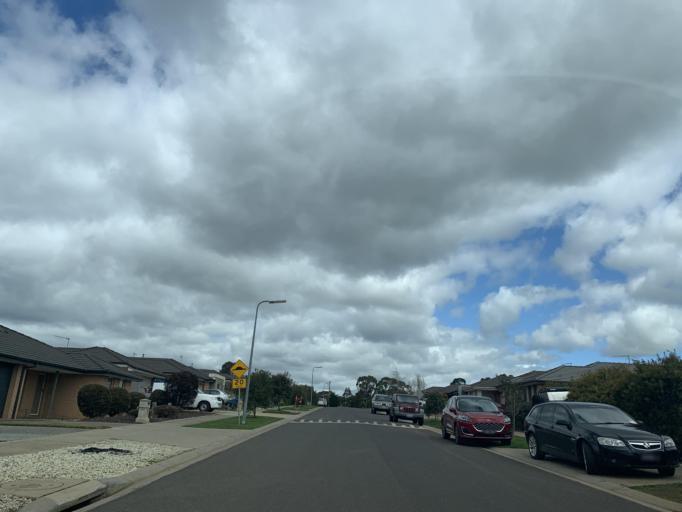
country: AU
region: Victoria
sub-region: Whittlesea
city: Whittlesea
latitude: -37.2921
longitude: 144.9355
